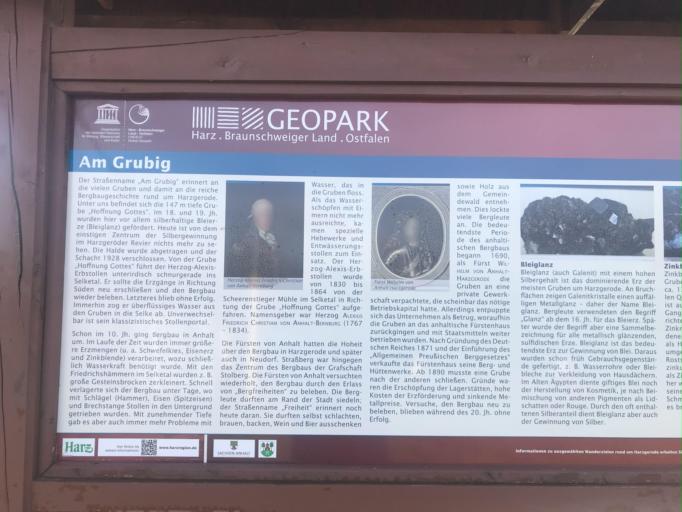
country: DE
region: Saxony-Anhalt
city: Harzgerode
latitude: 51.6493
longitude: 11.1447
